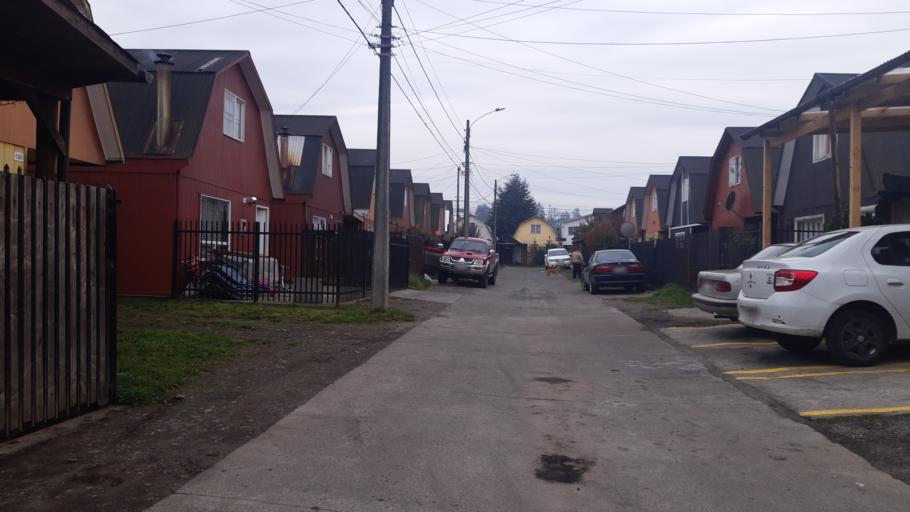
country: CL
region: Araucania
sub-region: Provincia de Cautin
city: Villarrica
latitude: -39.3081
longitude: -72.2165
